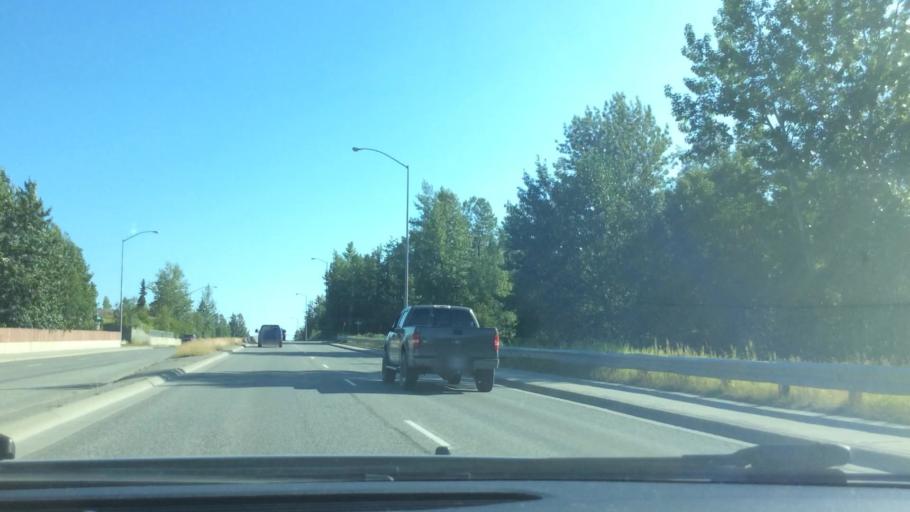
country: US
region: Alaska
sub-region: Anchorage Municipality
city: Anchorage
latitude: 61.1893
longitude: -149.7784
